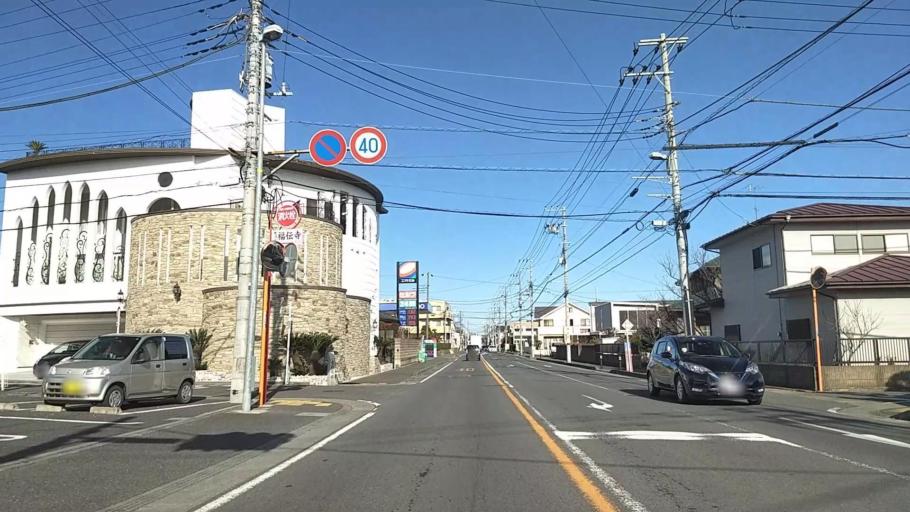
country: JP
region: Kanagawa
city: Atsugi
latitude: 35.4561
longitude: 139.3482
